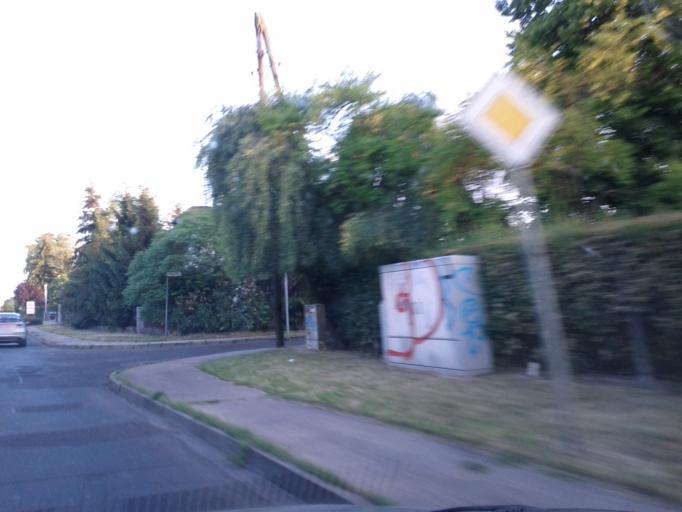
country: DE
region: Berlin
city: Hellersdorf
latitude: 52.5364
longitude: 13.6404
